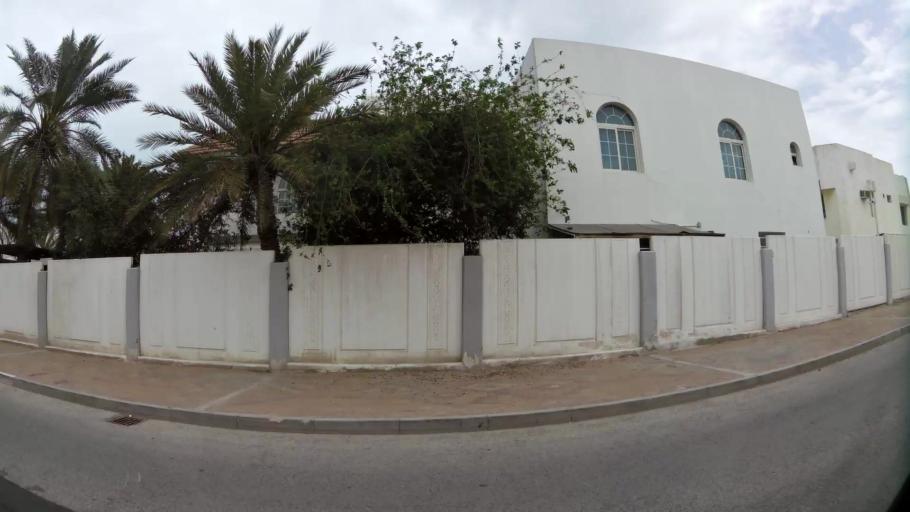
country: QA
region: Baladiyat ad Dawhah
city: Doha
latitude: 25.3315
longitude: 51.5030
